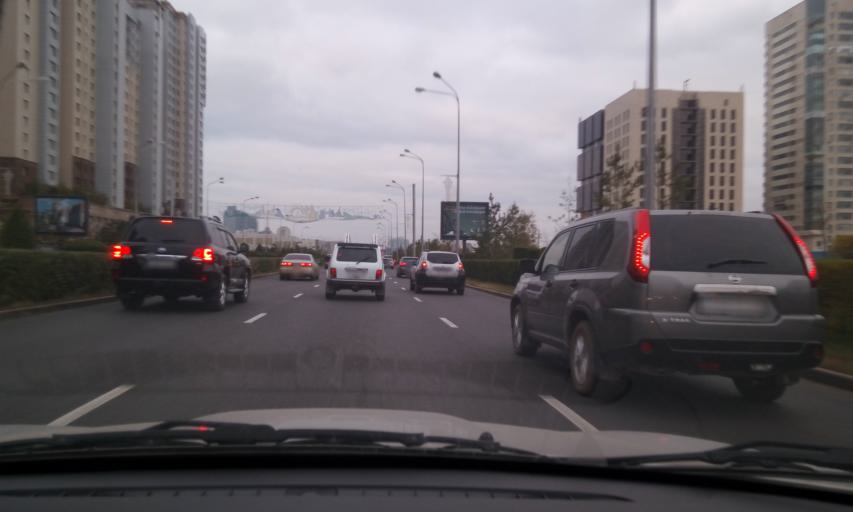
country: KZ
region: Astana Qalasy
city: Astana
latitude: 51.1290
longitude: 71.4623
